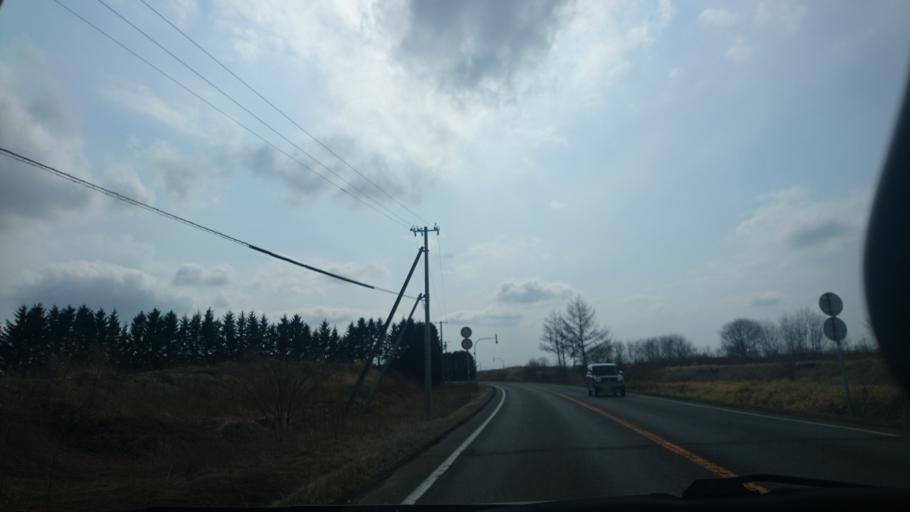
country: JP
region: Hokkaido
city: Otofuke
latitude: 43.1613
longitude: 143.2487
